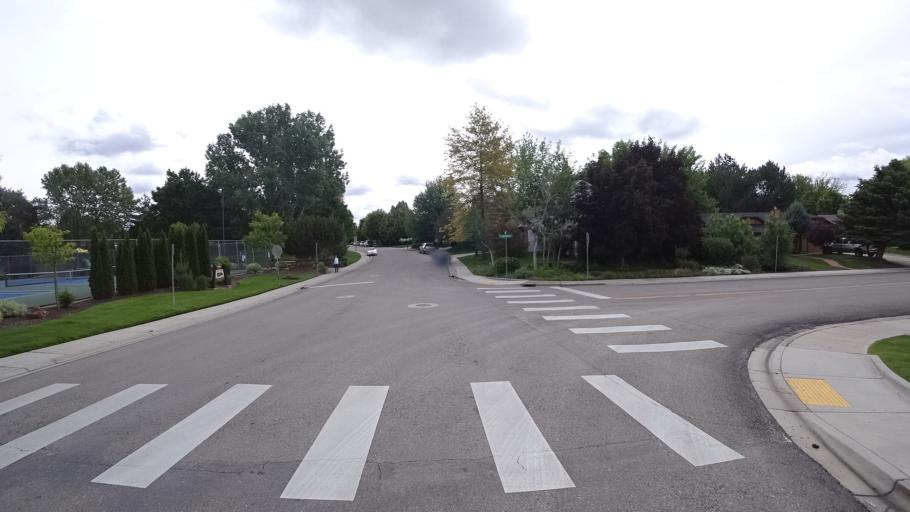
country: US
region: Idaho
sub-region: Ada County
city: Eagle
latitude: 43.7023
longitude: -116.3459
